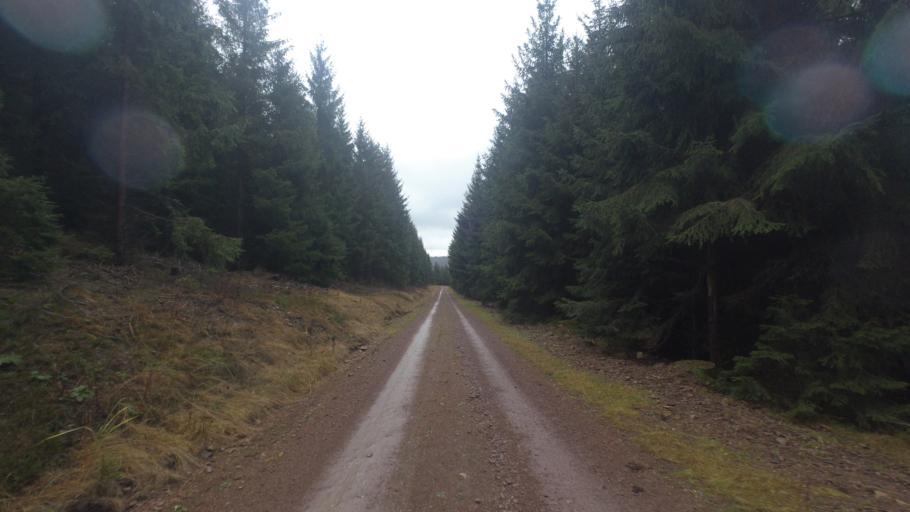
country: DE
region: Thuringia
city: Frankenhain
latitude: 50.7240
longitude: 10.7733
